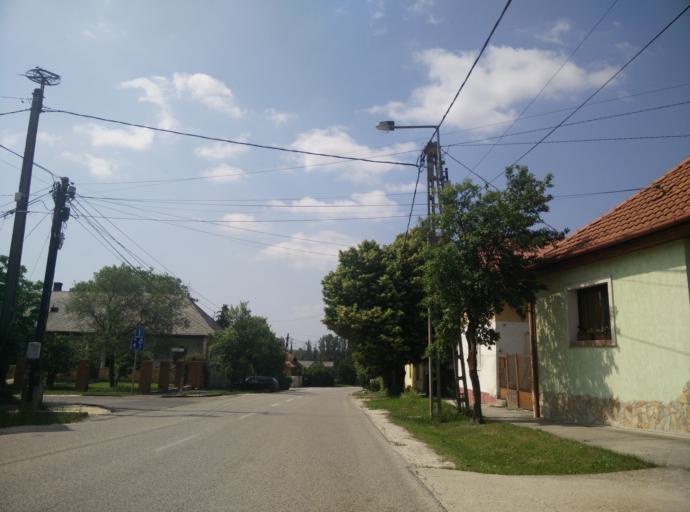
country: HU
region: Pest
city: Biatorbagy
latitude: 47.4662
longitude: 18.8032
